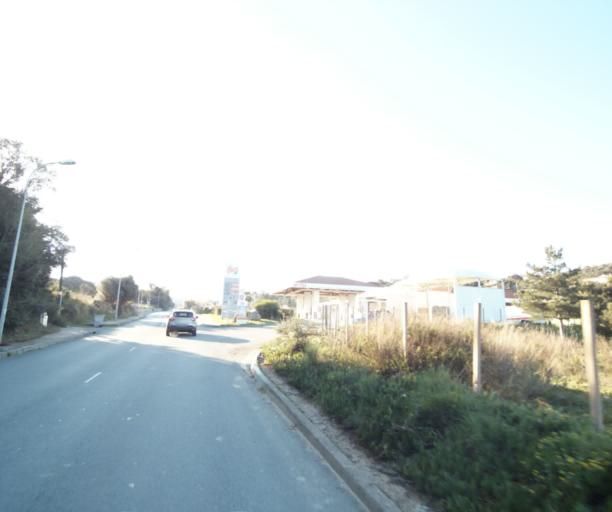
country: FR
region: Corsica
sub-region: Departement de la Corse-du-Sud
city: Propriano
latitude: 41.6726
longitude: 8.9084
